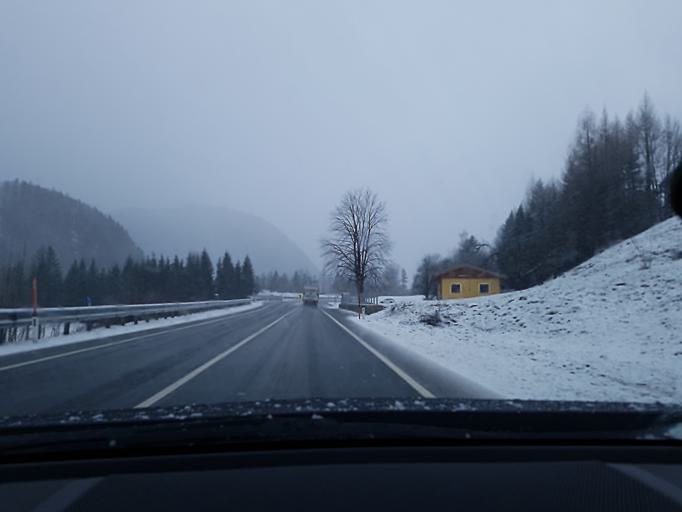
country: AT
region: Salzburg
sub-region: Politischer Bezirk Hallein
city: Scheffau am Tennengebirge
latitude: 47.5827
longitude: 13.2394
